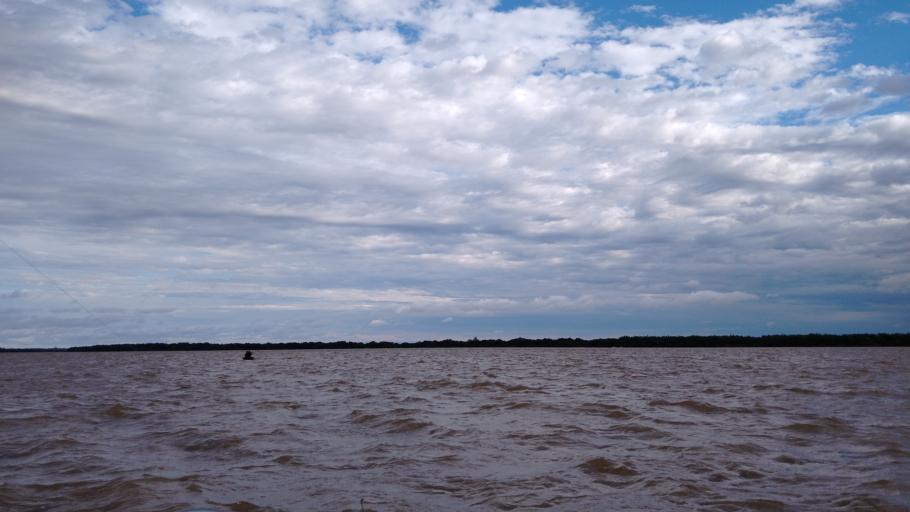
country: AR
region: Corrientes
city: Ituzaingo
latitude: -27.5148
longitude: -56.7038
